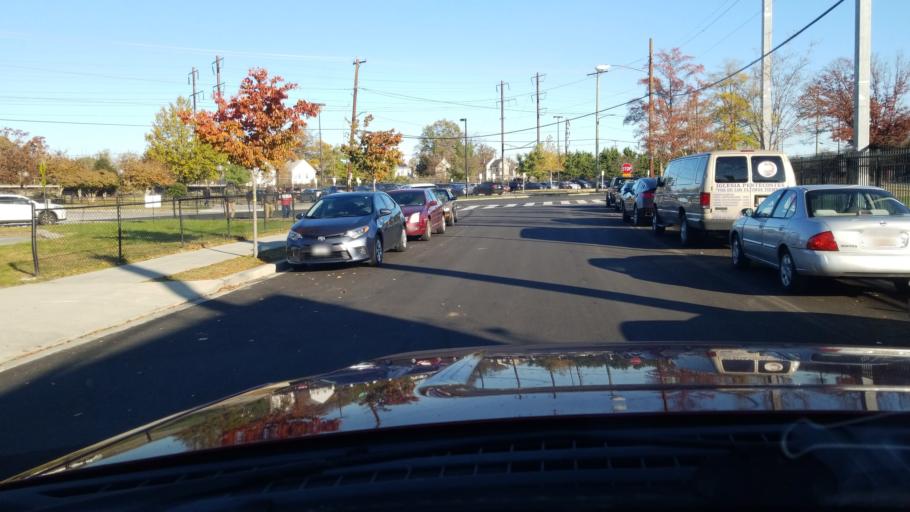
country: US
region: Maryland
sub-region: Prince George's County
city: Fairmount Heights
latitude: 38.9078
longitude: -76.9338
